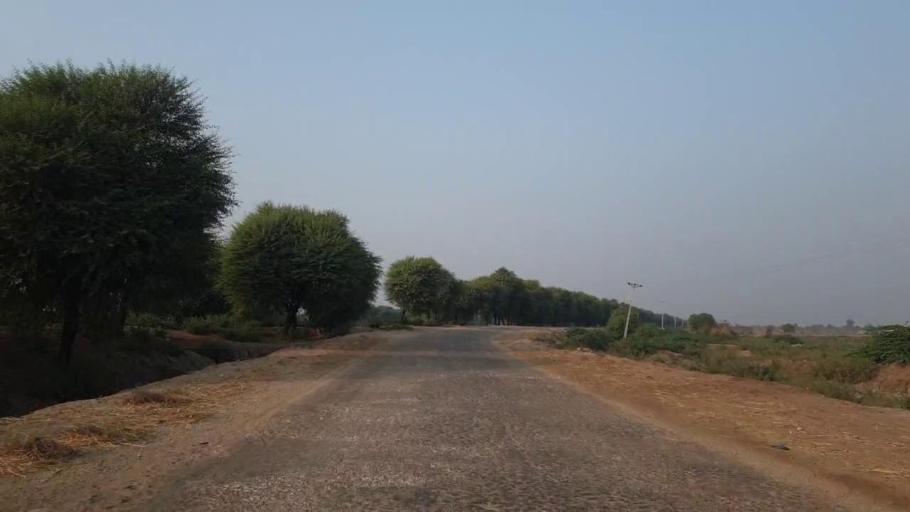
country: PK
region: Sindh
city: Tando Muhammad Khan
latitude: 25.1189
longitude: 68.4283
